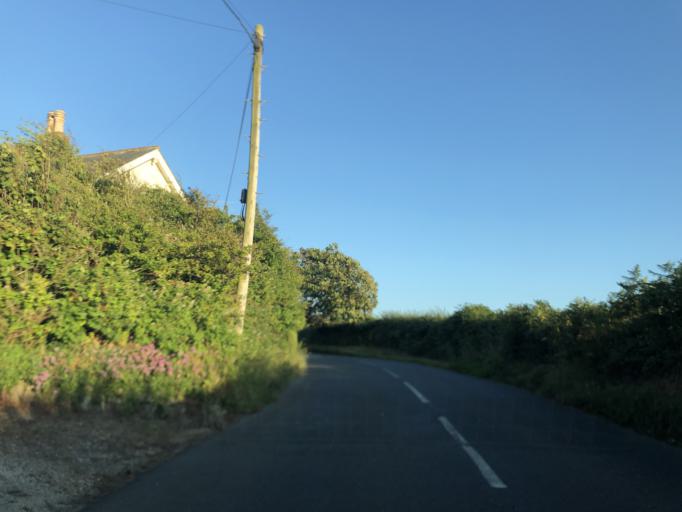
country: GB
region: England
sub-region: Isle of Wight
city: Chale
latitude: 50.6077
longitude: -1.3188
